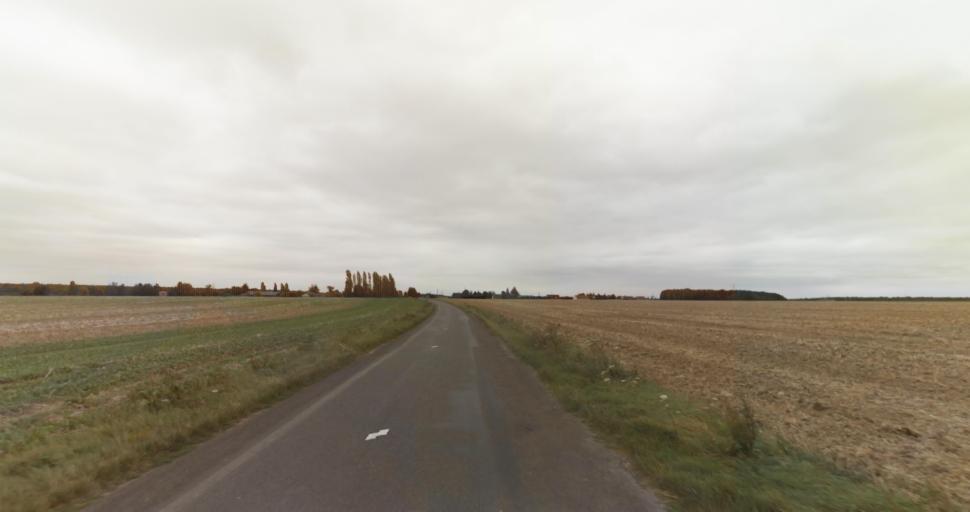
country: FR
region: Haute-Normandie
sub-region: Departement de l'Eure
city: La Couture-Boussey
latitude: 48.9177
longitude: 1.4044
